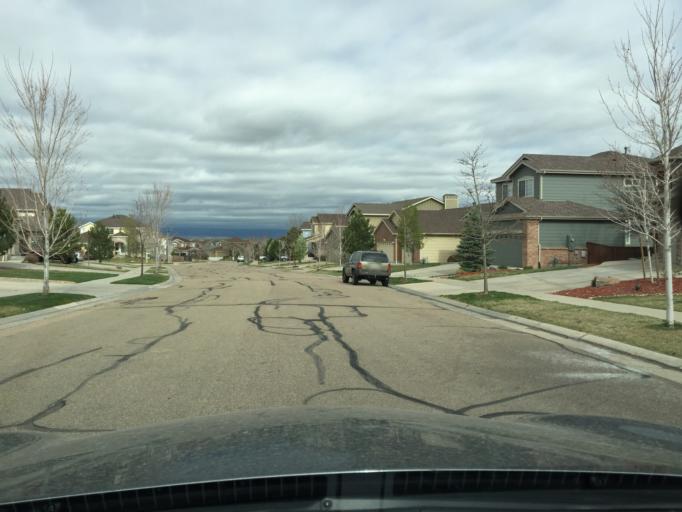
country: US
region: Colorado
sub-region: Boulder County
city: Erie
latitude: 40.0117
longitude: -105.0163
